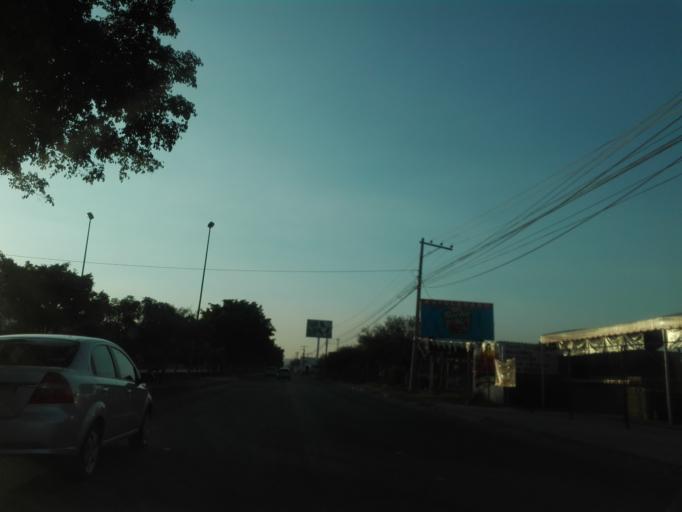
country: MX
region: Guanajuato
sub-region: Leon
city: Medina
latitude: 21.1257
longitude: -101.6330
